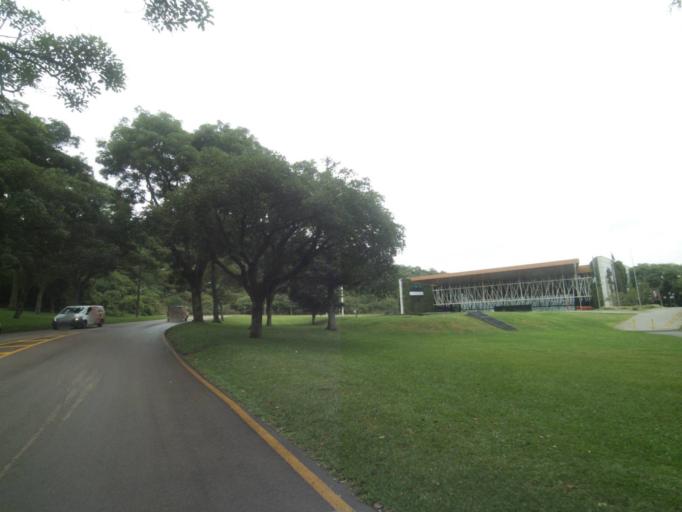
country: BR
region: Parana
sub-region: Curitiba
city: Curitiba
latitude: -25.4288
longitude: -49.3148
